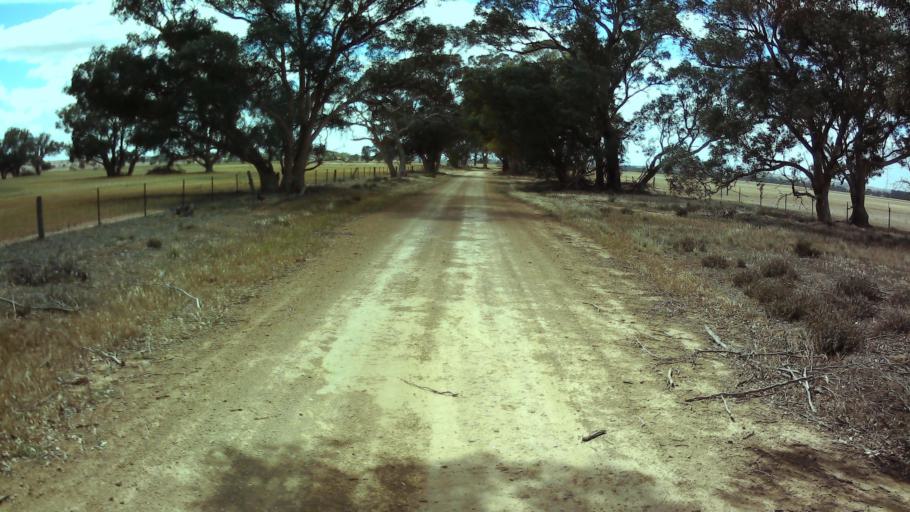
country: AU
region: New South Wales
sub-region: Weddin
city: Grenfell
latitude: -33.9979
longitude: 148.2963
